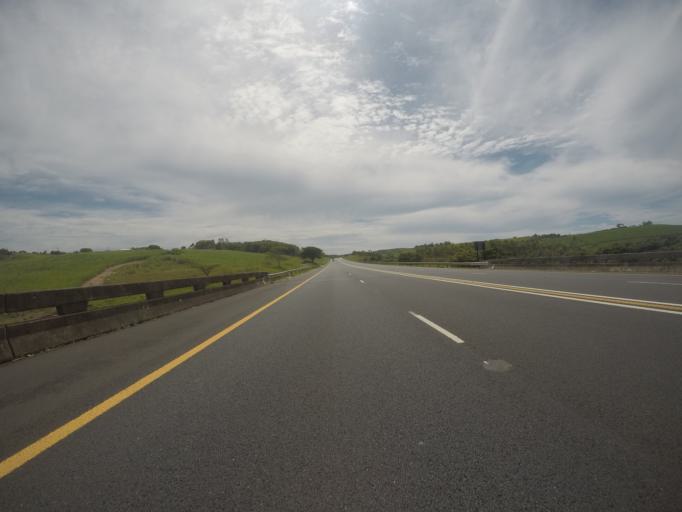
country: ZA
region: KwaZulu-Natal
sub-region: iLembe District Municipality
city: Mandeni
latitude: -29.1690
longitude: 31.5218
